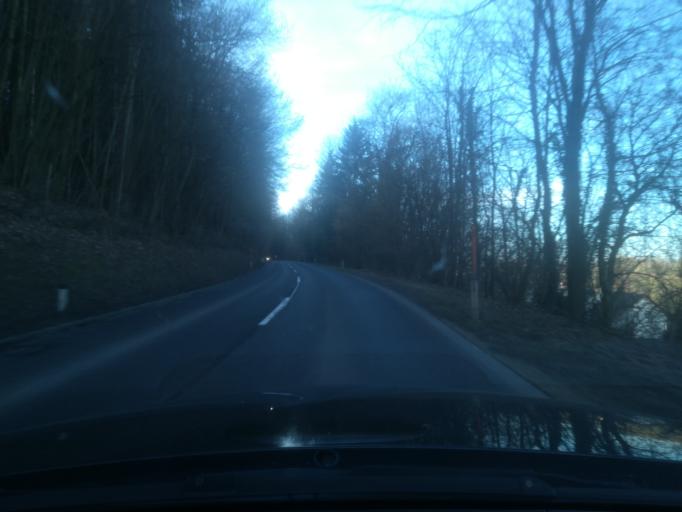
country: AT
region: Upper Austria
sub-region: Wels-Land
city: Marchtrenk
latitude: 48.1626
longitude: 14.0867
